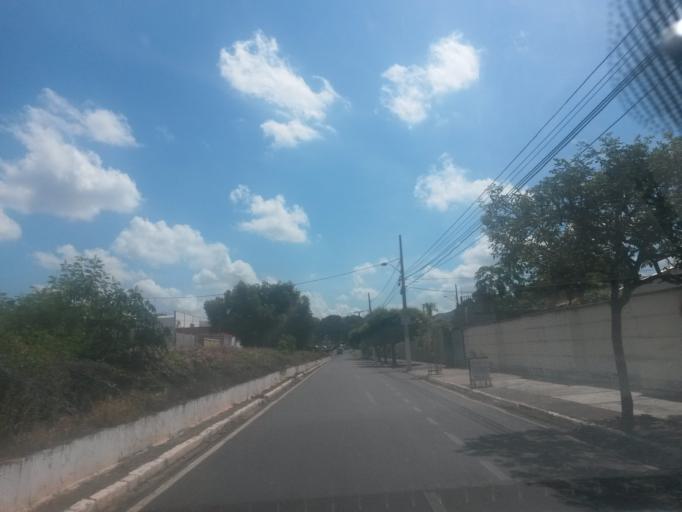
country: BR
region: Mato Grosso
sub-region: Cuiaba
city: Cuiaba
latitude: -15.6005
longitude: -56.0846
